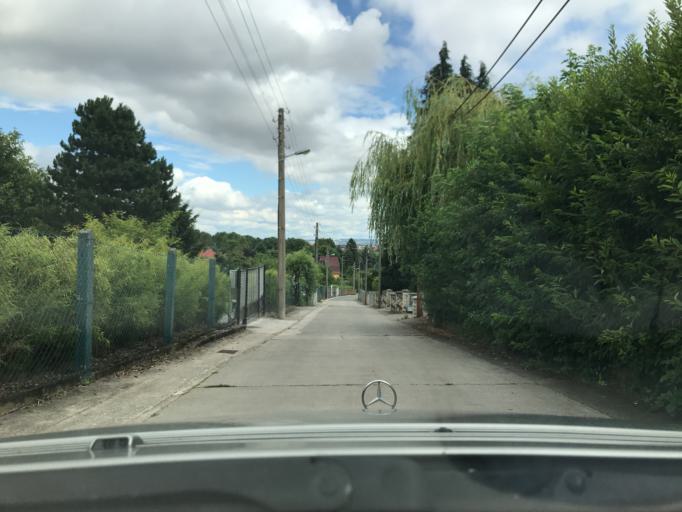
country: DE
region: Thuringia
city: Muehlhausen
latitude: 51.2109
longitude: 10.4321
